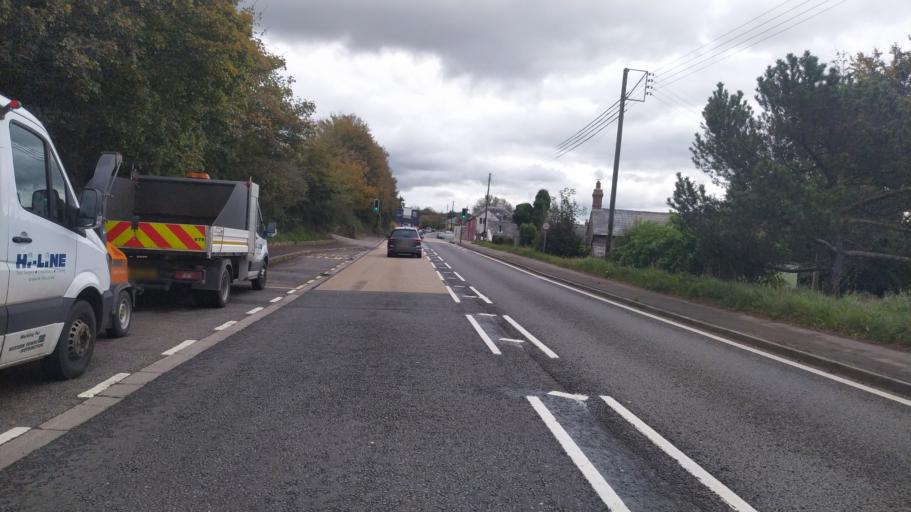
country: GB
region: England
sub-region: Dorset
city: Bridport
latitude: 50.7409
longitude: -2.8447
